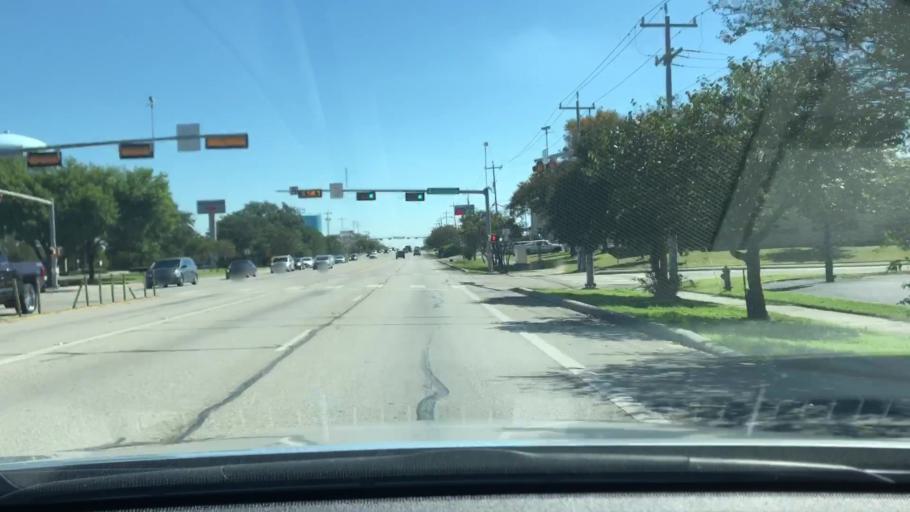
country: US
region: Texas
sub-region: Bexar County
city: Live Oak
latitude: 29.5596
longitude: -98.3251
